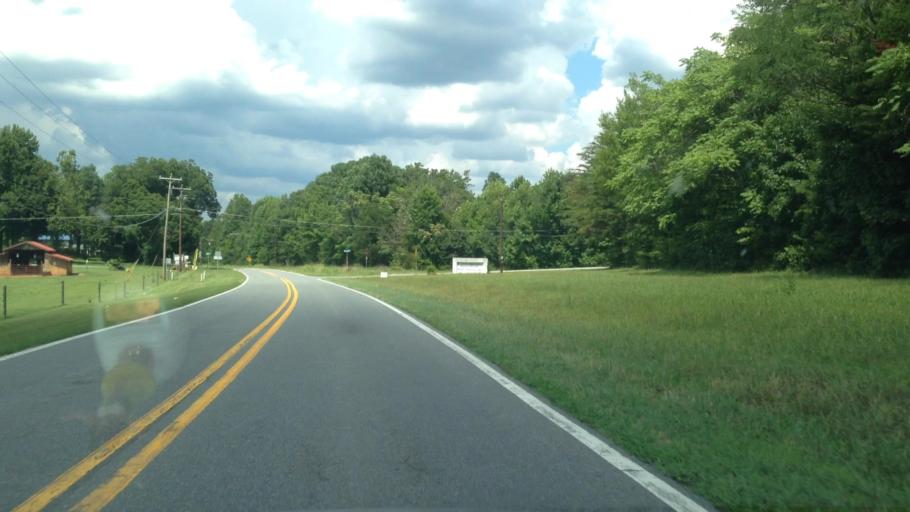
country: US
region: North Carolina
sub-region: Rockingham County
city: Reidsville
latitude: 36.4274
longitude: -79.5820
